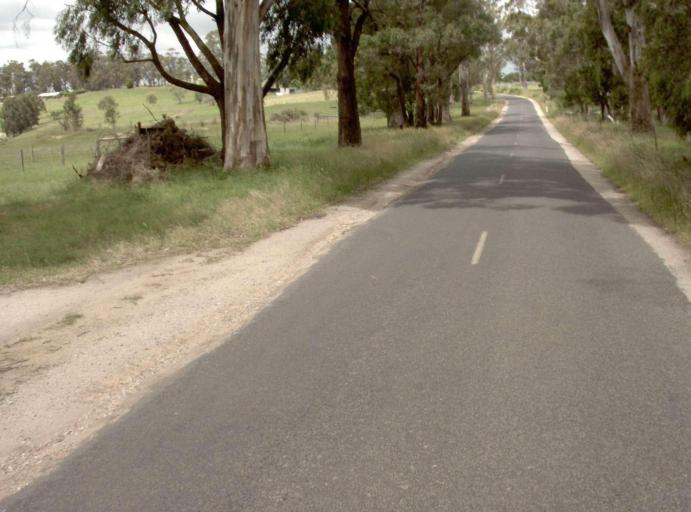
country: AU
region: Victoria
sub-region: Latrobe
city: Moe
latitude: -37.9979
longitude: 146.1459
